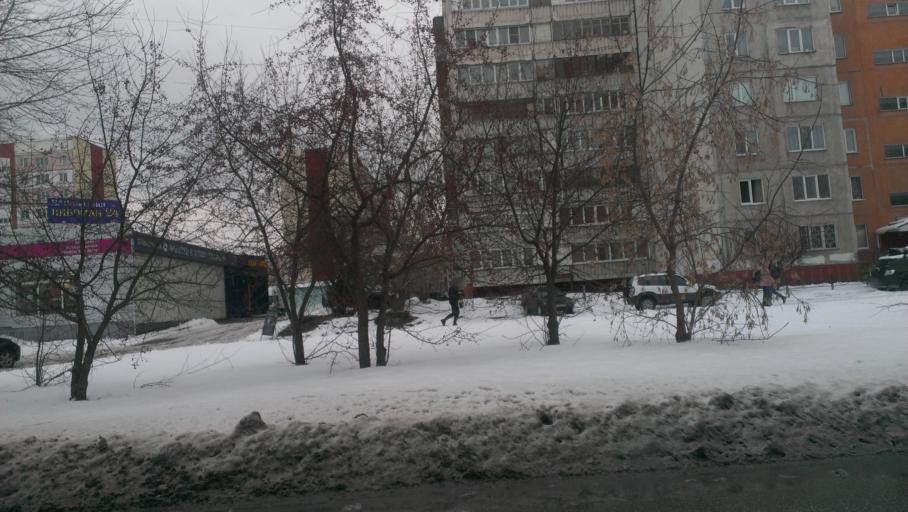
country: RU
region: Altai Krai
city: Novosilikatnyy
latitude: 53.3394
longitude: 83.6728
